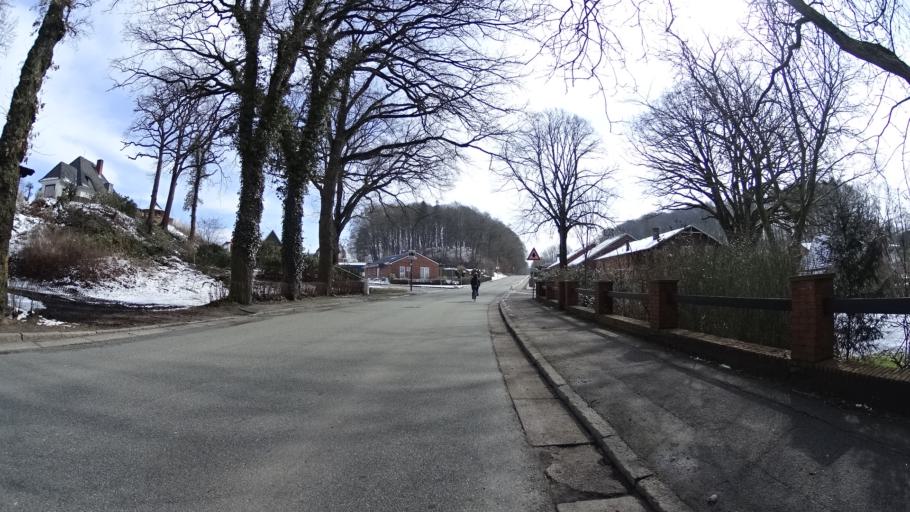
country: DE
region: Schleswig-Holstein
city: Boostedt
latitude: 54.0098
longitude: 10.0322
